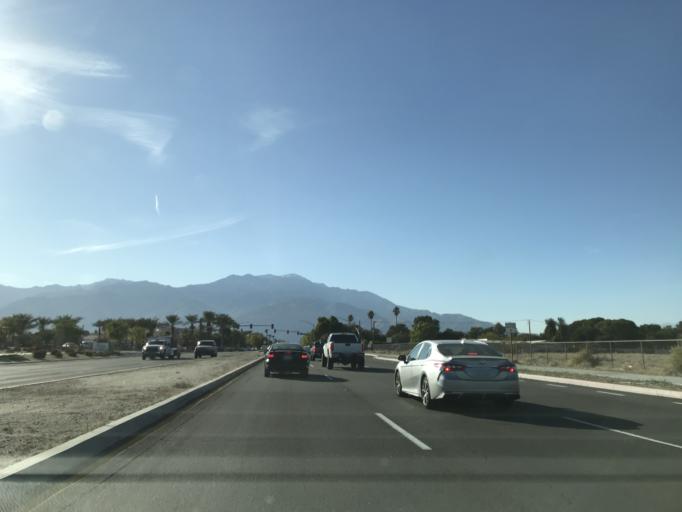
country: US
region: California
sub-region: Riverside County
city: Cathedral City
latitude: 33.8160
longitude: -116.4386
